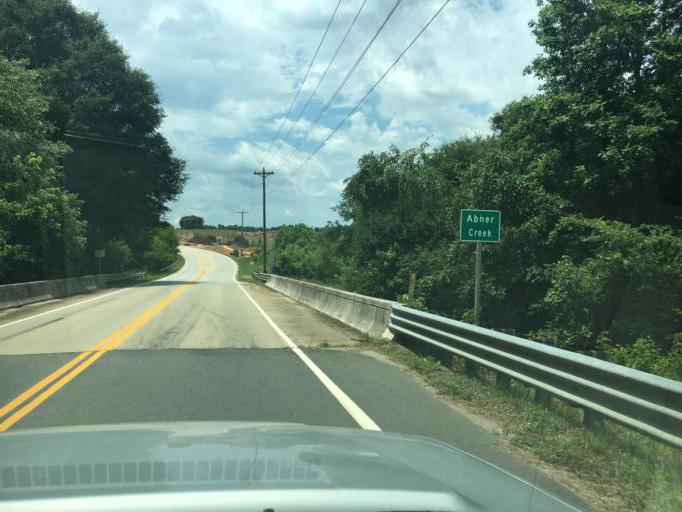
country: US
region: South Carolina
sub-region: Spartanburg County
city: Duncan
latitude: 34.8713
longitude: -82.1603
